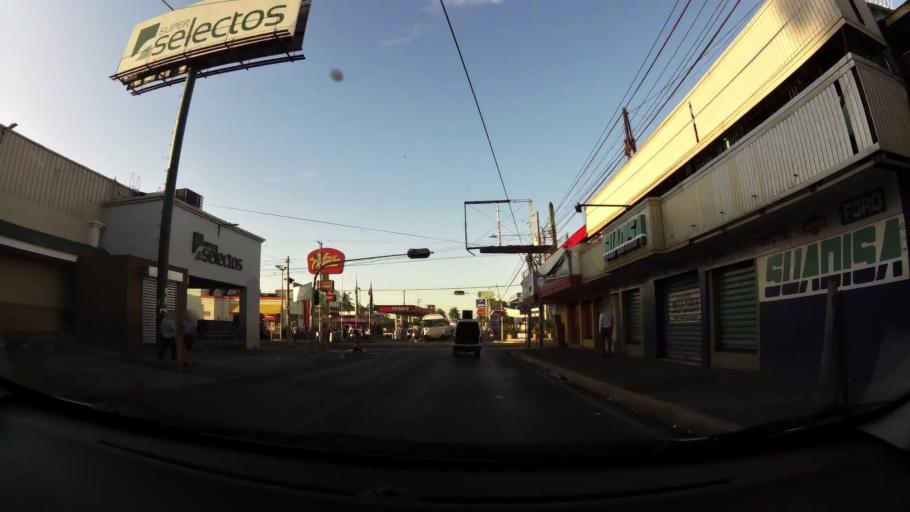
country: SV
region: Sonsonate
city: Sonsonate
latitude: 13.7175
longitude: -89.7228
